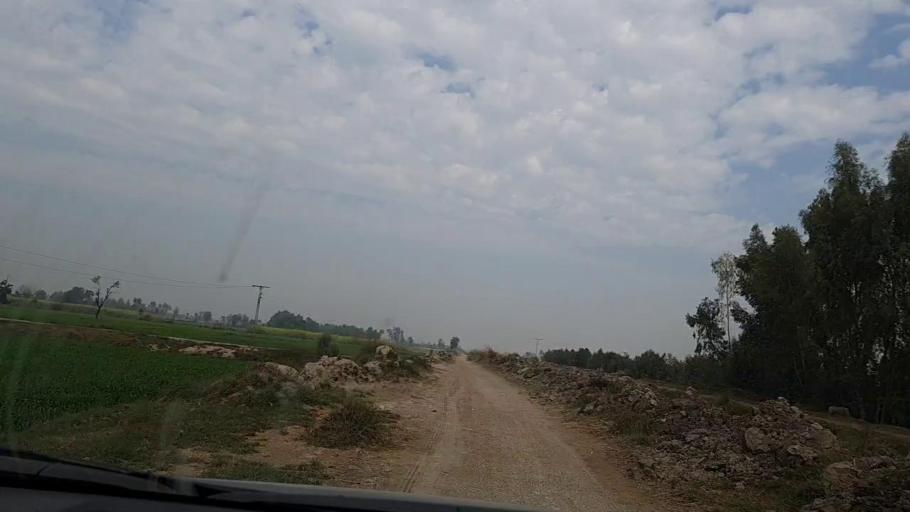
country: PK
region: Sindh
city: Daulatpur
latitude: 26.5613
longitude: 67.9831
